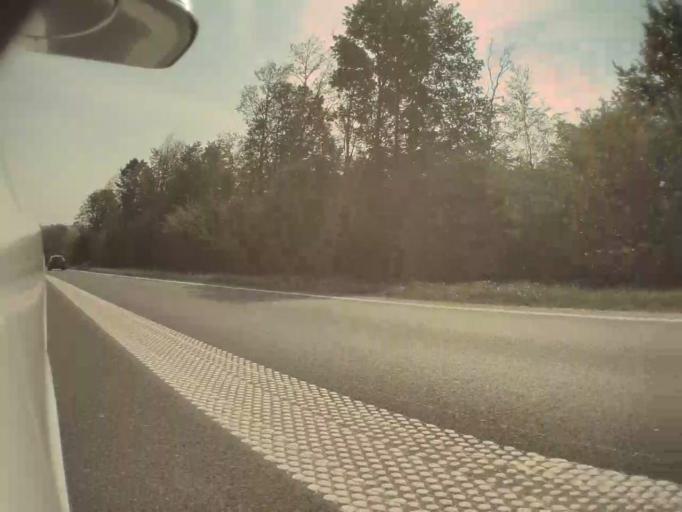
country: BE
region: Wallonia
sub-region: Province de Namur
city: Ciney
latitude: 50.3084
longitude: 5.1226
